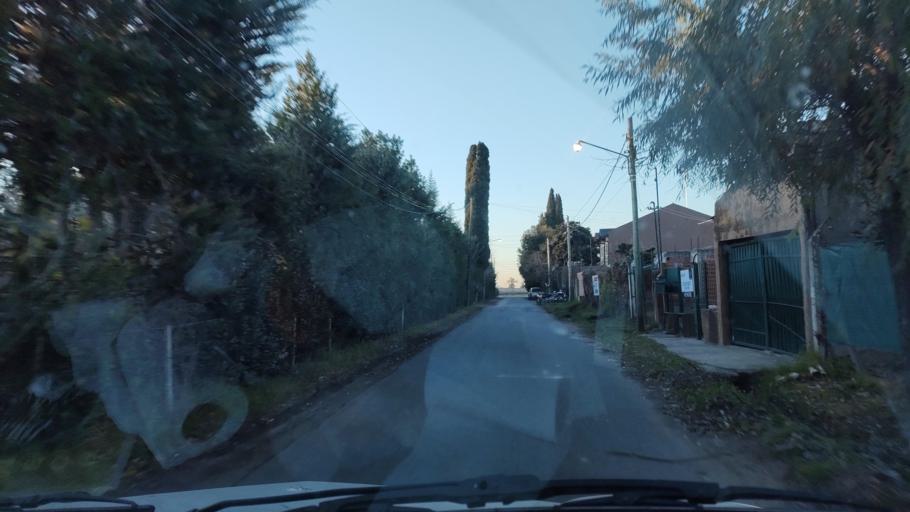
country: AR
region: Buenos Aires
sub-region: Partido de La Plata
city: La Plata
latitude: -34.9037
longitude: -58.0516
